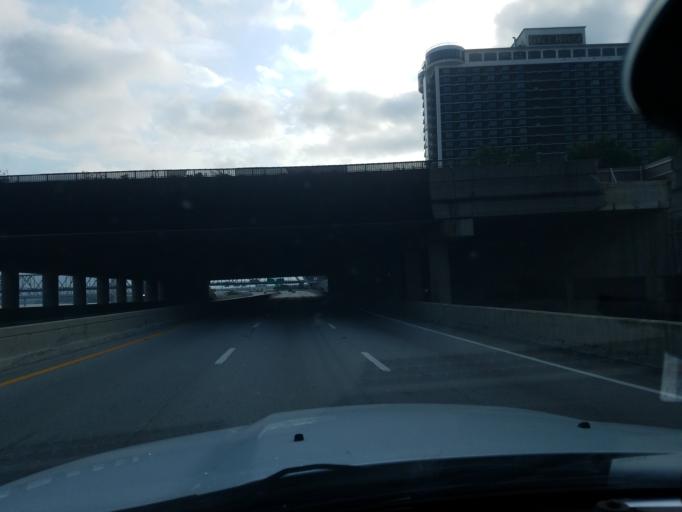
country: US
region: Kentucky
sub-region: Jefferson County
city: Louisville
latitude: 38.2589
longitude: -85.7585
